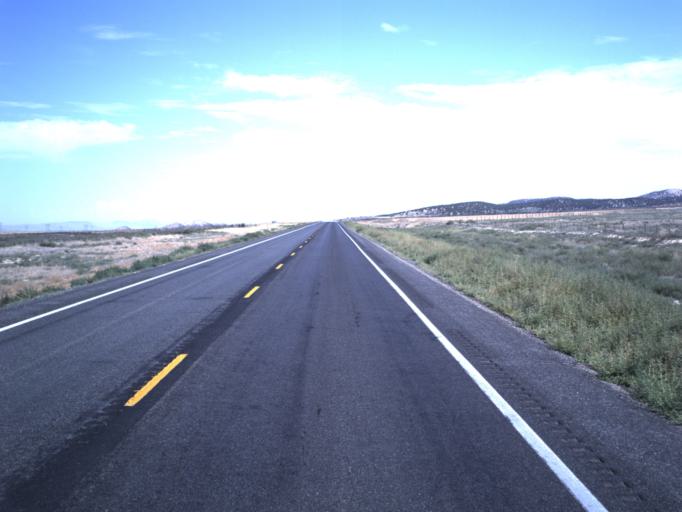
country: US
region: Utah
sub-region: Sanpete County
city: Gunnison
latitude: 39.3030
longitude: -111.8951
